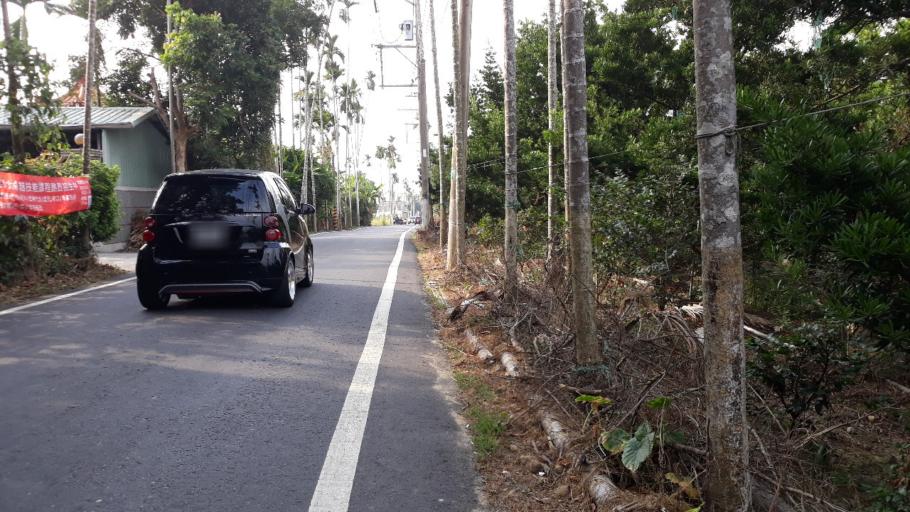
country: TW
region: Taiwan
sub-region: Chiayi
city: Jiayi Shi
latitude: 23.4299
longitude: 120.5215
